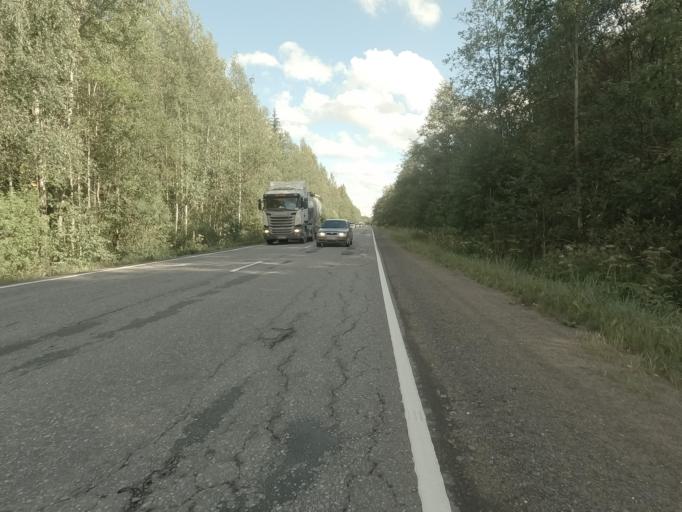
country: RU
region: Leningrad
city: Shcheglovo
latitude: 59.9943
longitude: 30.8788
